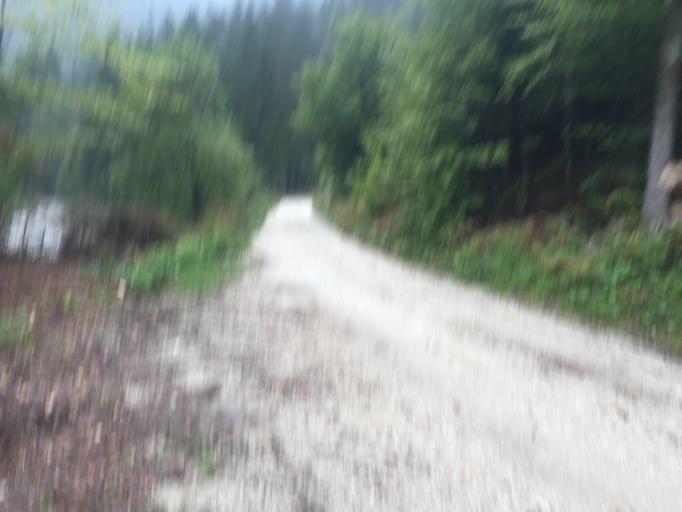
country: IT
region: Friuli Venezia Giulia
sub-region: Provincia di Udine
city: Tarvisio
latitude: 46.4831
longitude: 13.6116
